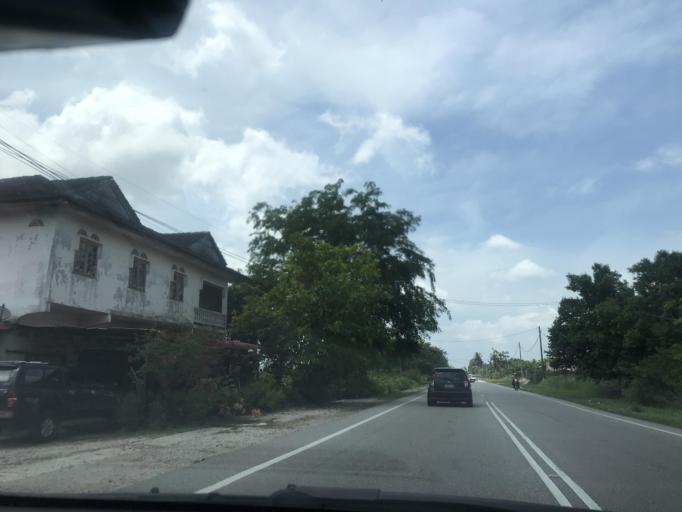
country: MY
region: Kelantan
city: Kota Bharu
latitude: 6.1490
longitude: 102.2139
